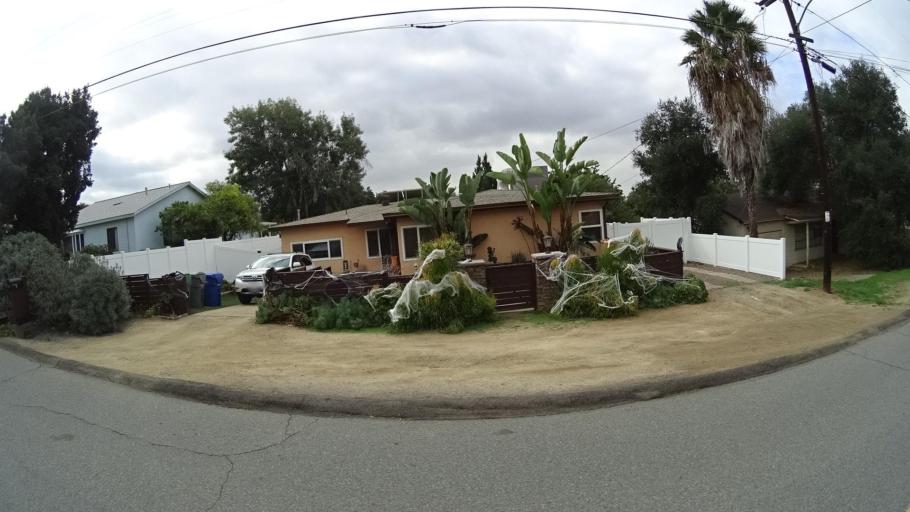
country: US
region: California
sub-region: San Diego County
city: Spring Valley
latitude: 32.7526
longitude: -116.9984
